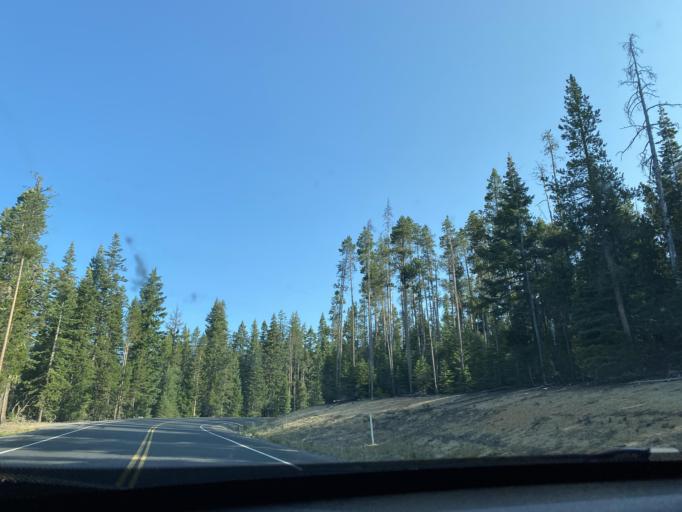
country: US
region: Oregon
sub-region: Deschutes County
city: Three Rivers
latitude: 43.7080
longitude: -121.2849
